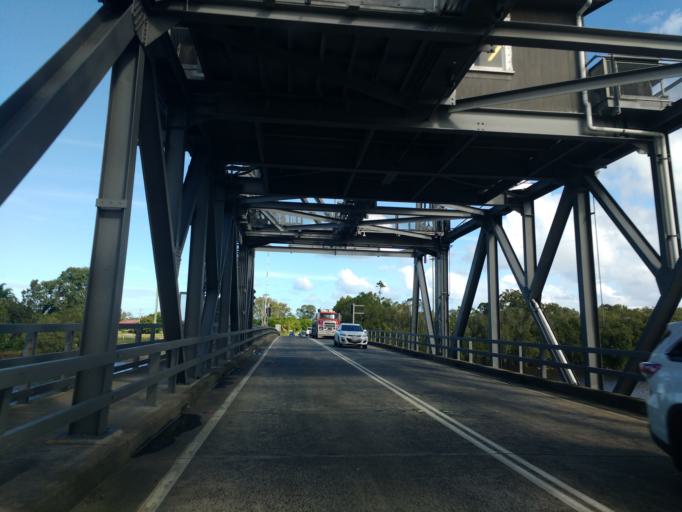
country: AU
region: New South Wales
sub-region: Ballina
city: Ballina
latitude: -28.9534
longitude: 153.4647
